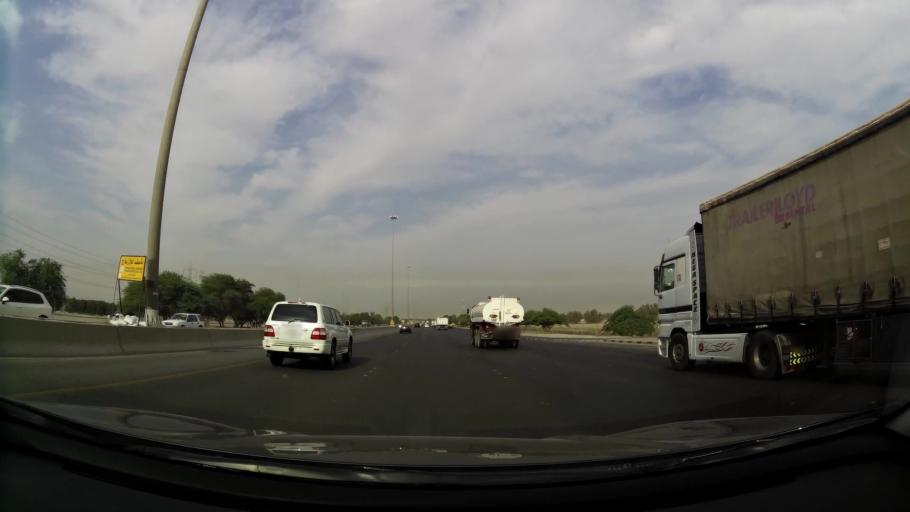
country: KW
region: Al Asimah
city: Ar Rabiyah
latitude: 29.2779
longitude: 47.8017
